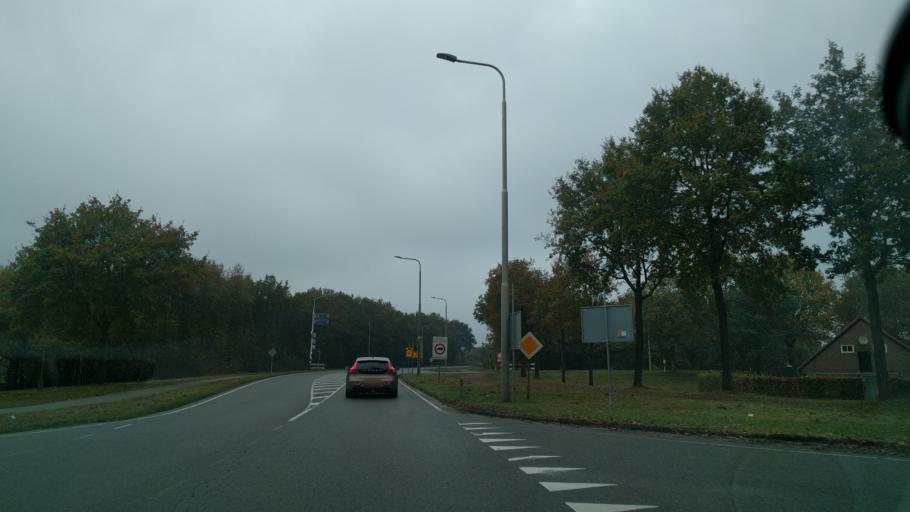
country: NL
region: North Brabant
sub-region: Gemeente Rucphen
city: Rucphen
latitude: 51.5492
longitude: 4.5466
